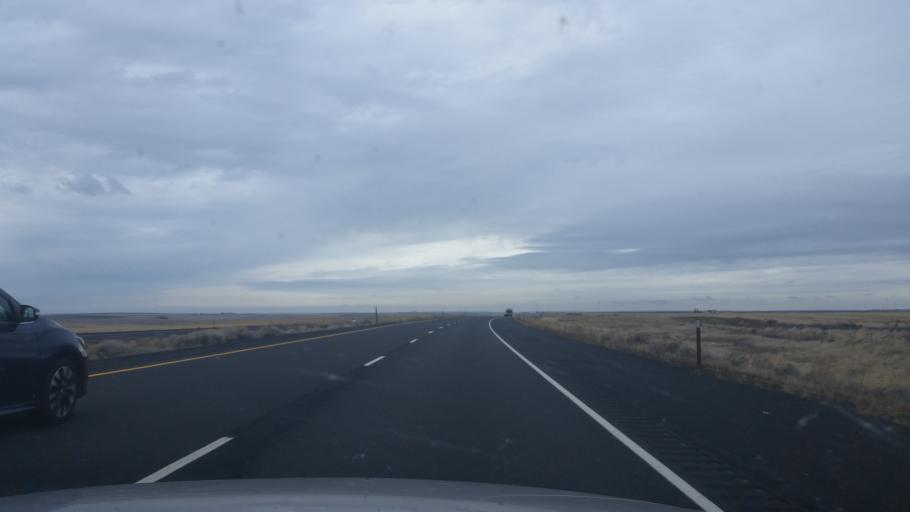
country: US
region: Washington
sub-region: Grant County
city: Warden
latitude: 47.0867
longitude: -118.7198
